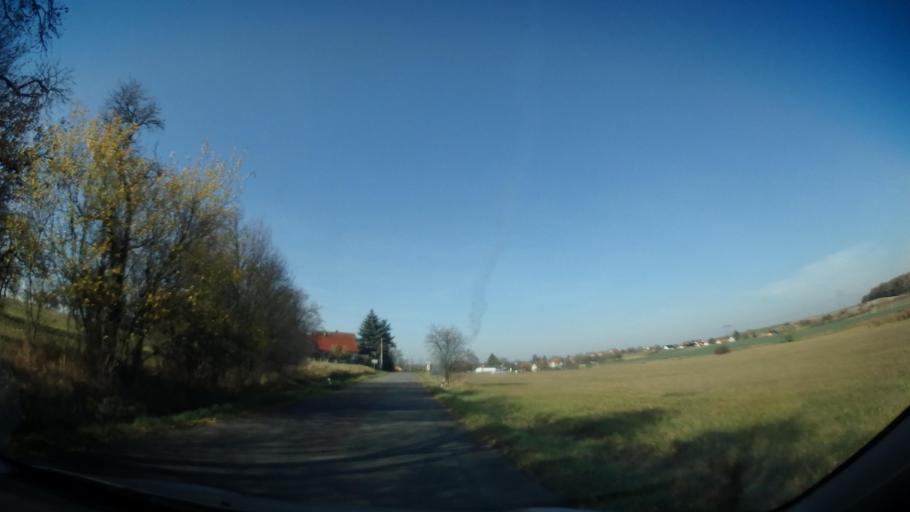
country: CZ
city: Ceske Mezirici
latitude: 50.2468
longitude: 16.0177
